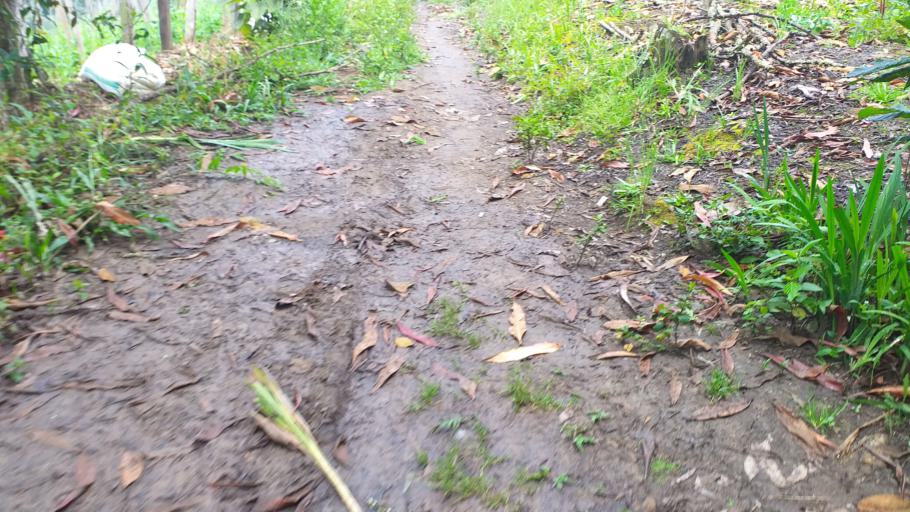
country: CO
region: Cundinamarca
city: Tenza
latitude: 5.1123
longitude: -73.4496
